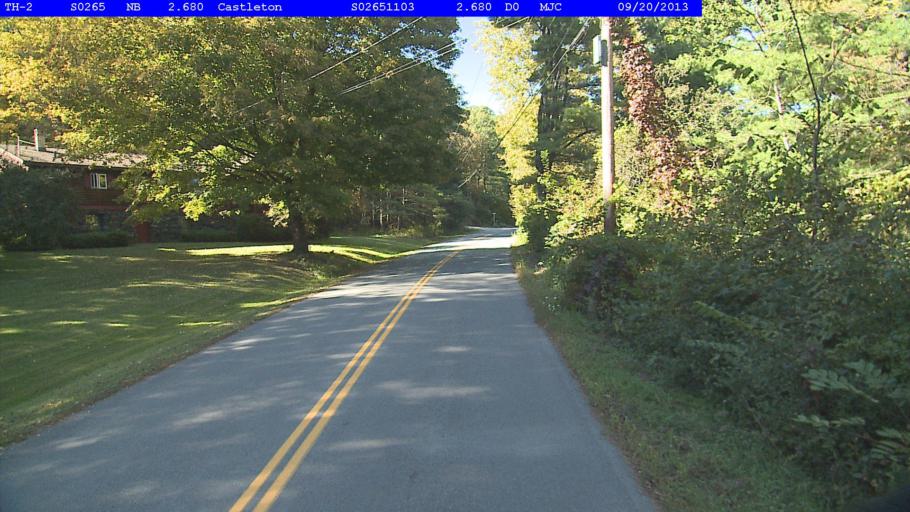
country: US
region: Vermont
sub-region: Rutland County
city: Fair Haven
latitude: 43.6396
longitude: -73.2337
